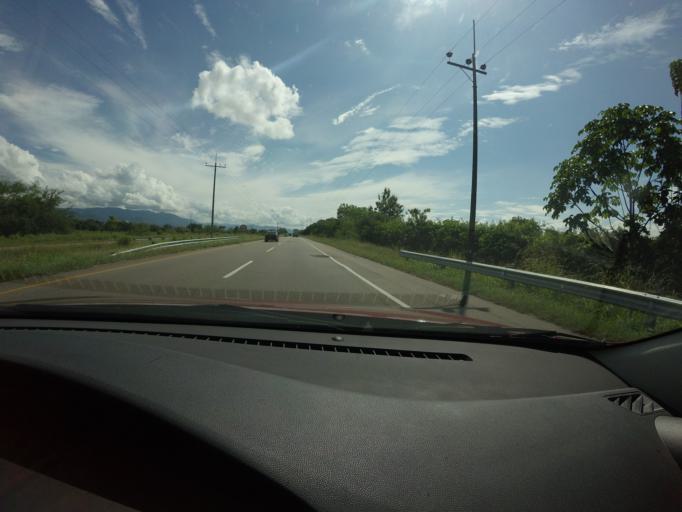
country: CO
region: Cundinamarca
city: Puerto Salgar
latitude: 5.6371
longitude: -74.6182
